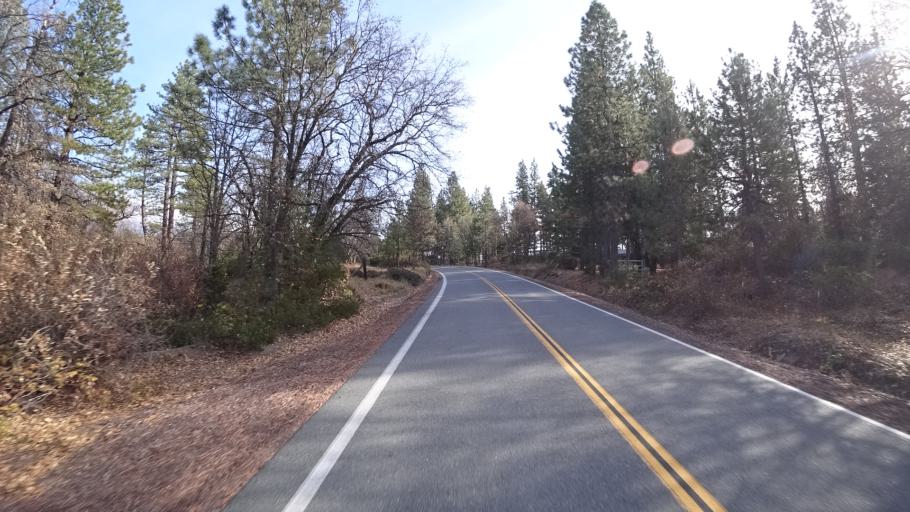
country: US
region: California
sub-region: Siskiyou County
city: Weed
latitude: 41.4026
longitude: -122.4256
